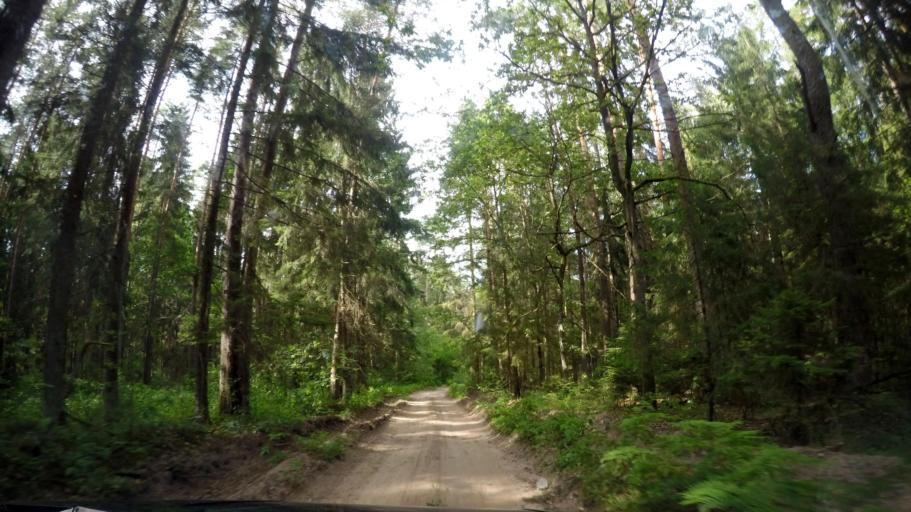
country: BY
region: Grodnenskaya
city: Skidal'
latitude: 53.8339
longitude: 24.1769
